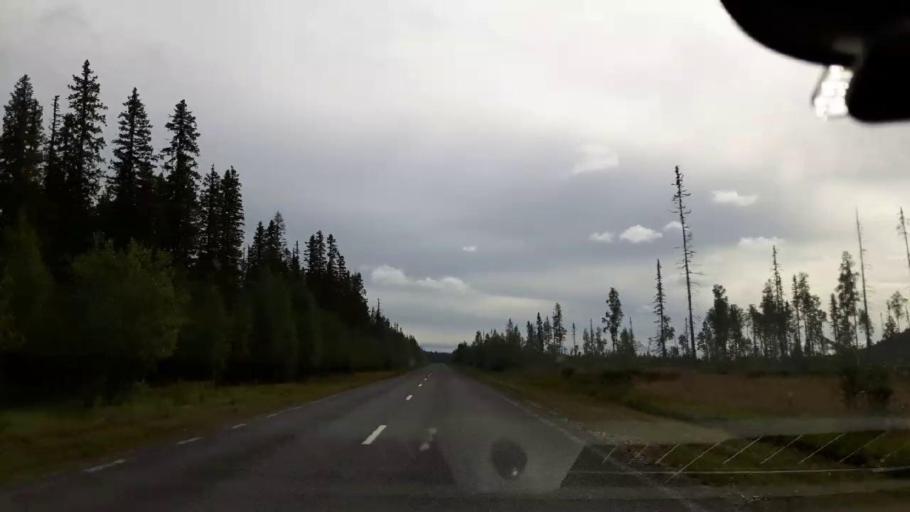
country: SE
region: Jaemtland
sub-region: Ragunda Kommun
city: Hammarstrand
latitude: 63.1268
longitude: 15.8925
